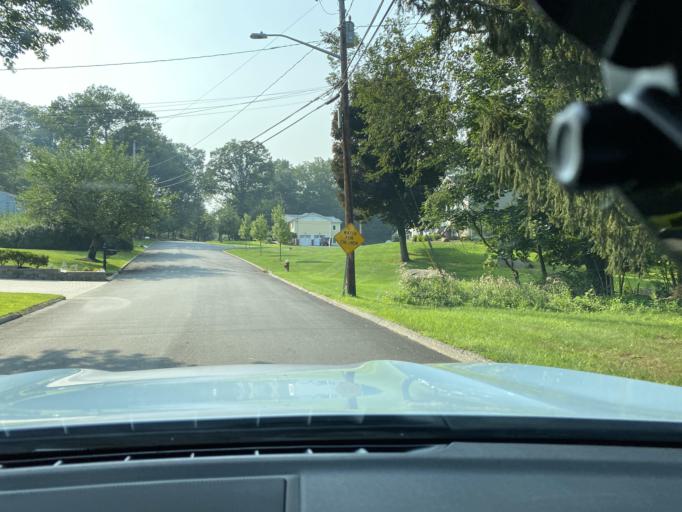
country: US
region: New York
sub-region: Rockland County
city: Airmont
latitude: 41.0858
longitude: -74.1225
